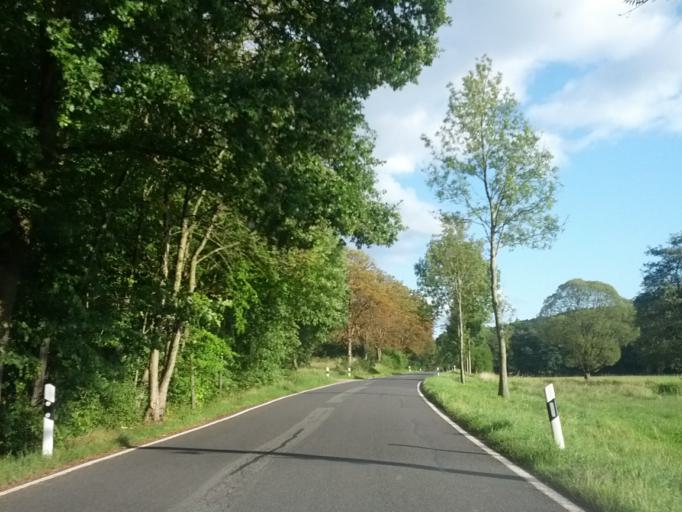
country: DE
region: Thuringia
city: Wolfsburg-Unkeroda
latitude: 50.9287
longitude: 10.2845
